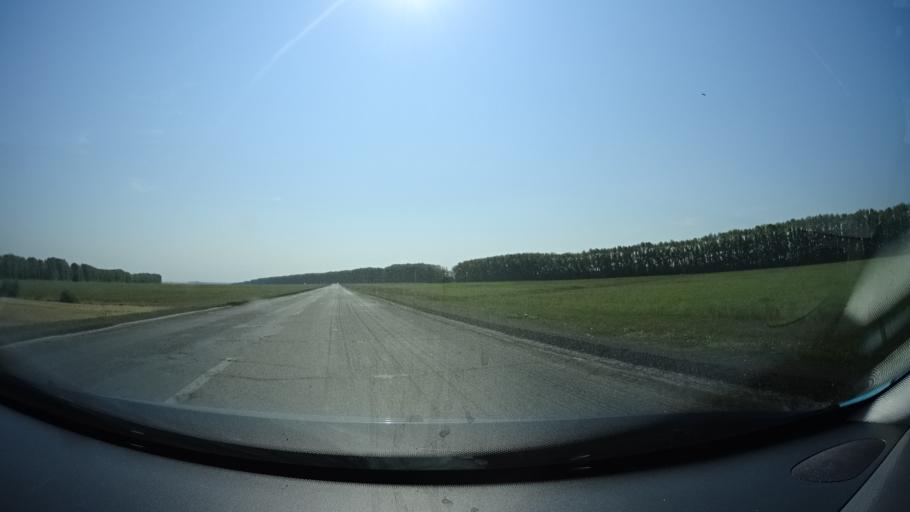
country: RU
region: Bashkortostan
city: Kabakovo
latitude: 54.4566
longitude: 55.9688
